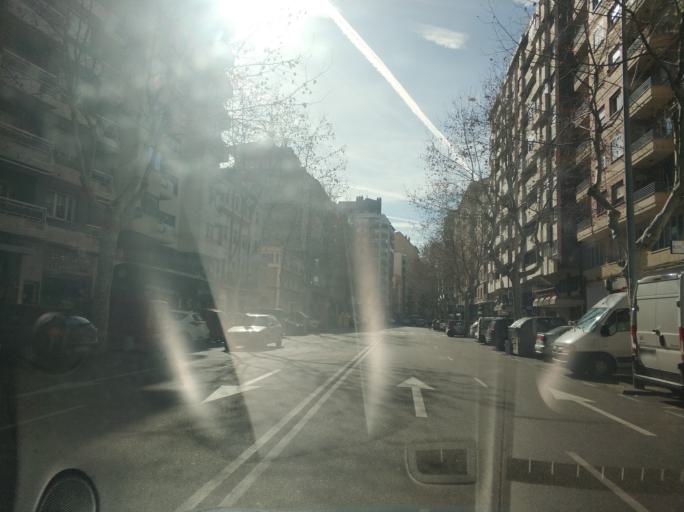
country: ES
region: Castille and Leon
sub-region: Provincia de Zamora
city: Zamora
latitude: 41.5109
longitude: -5.7414
